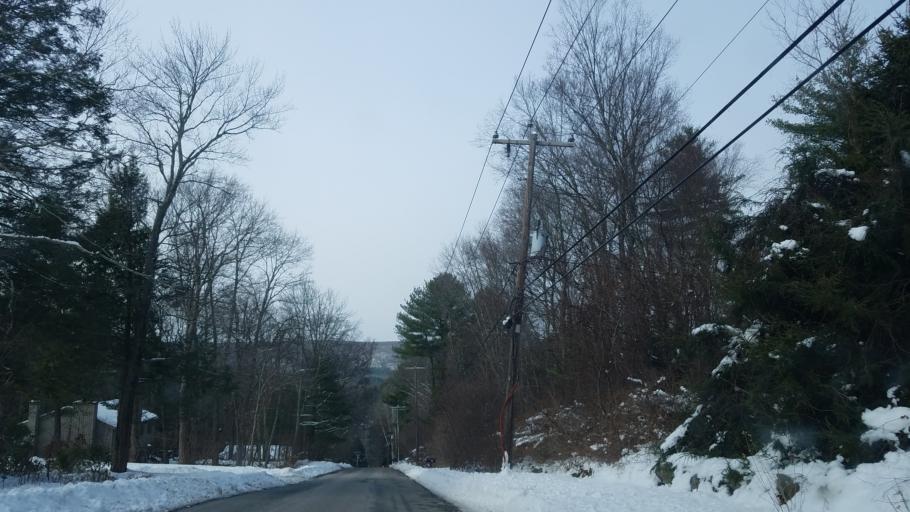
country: US
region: Connecticut
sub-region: Hartford County
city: Collinsville
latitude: 41.8401
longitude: -72.9220
